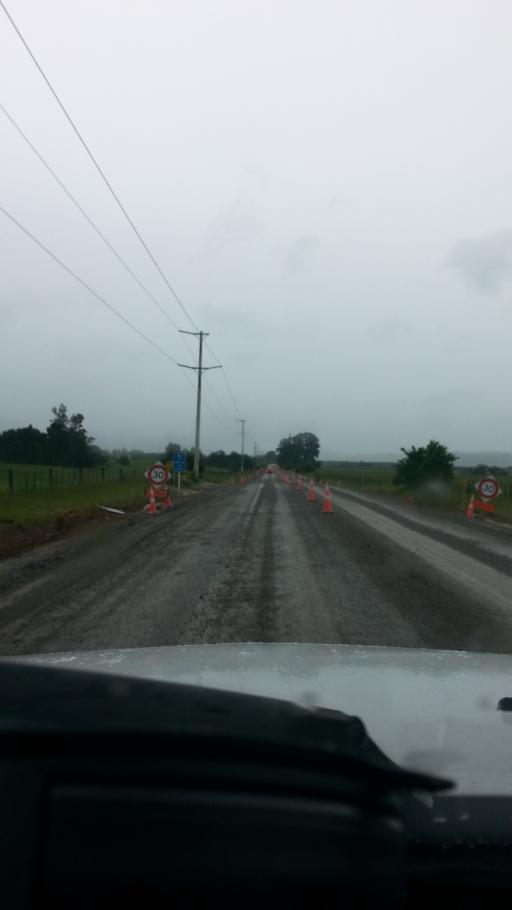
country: NZ
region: Wellington
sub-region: Masterton District
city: Masterton
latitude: -40.8330
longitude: 175.6281
